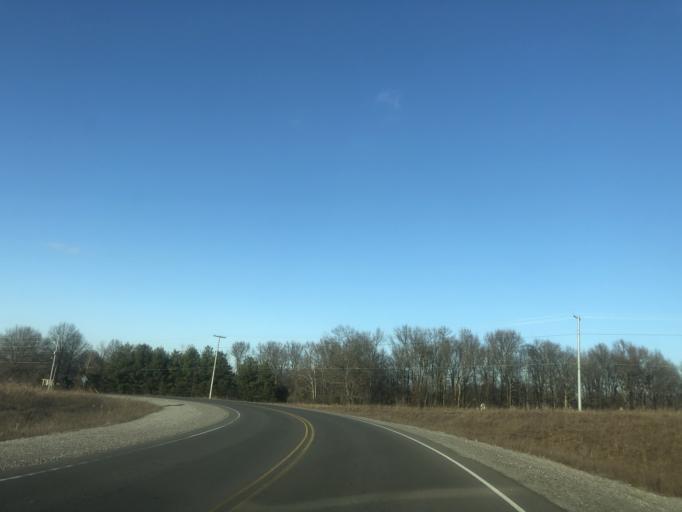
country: US
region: Tennessee
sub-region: Sumner County
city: Portland
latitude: 36.6224
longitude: -86.5553
